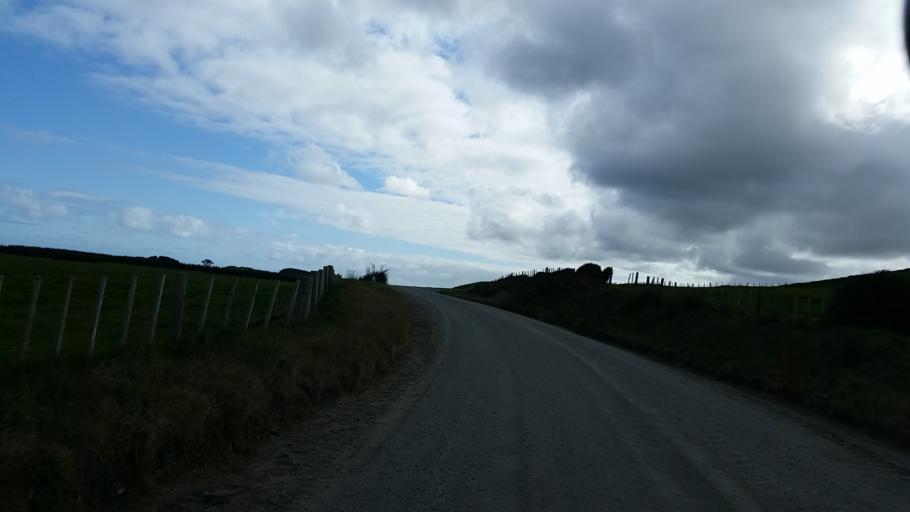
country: NZ
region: Taranaki
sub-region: South Taranaki District
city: Patea
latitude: -39.7926
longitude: 174.5847
